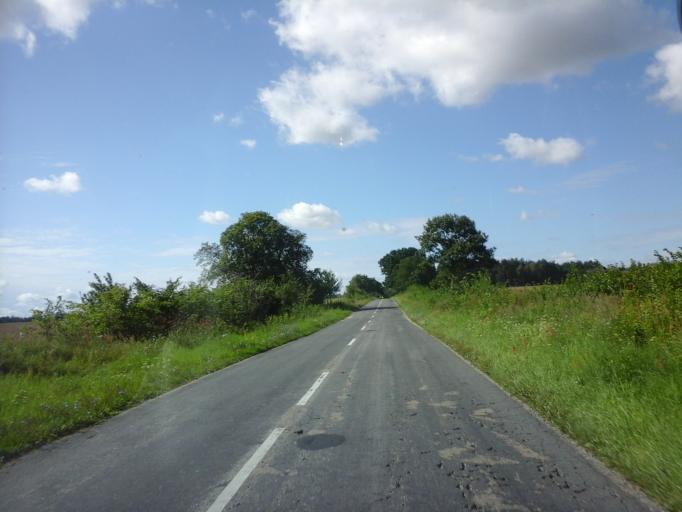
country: PL
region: West Pomeranian Voivodeship
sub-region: Powiat stargardzki
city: Suchan
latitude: 53.2101
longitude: 15.2847
